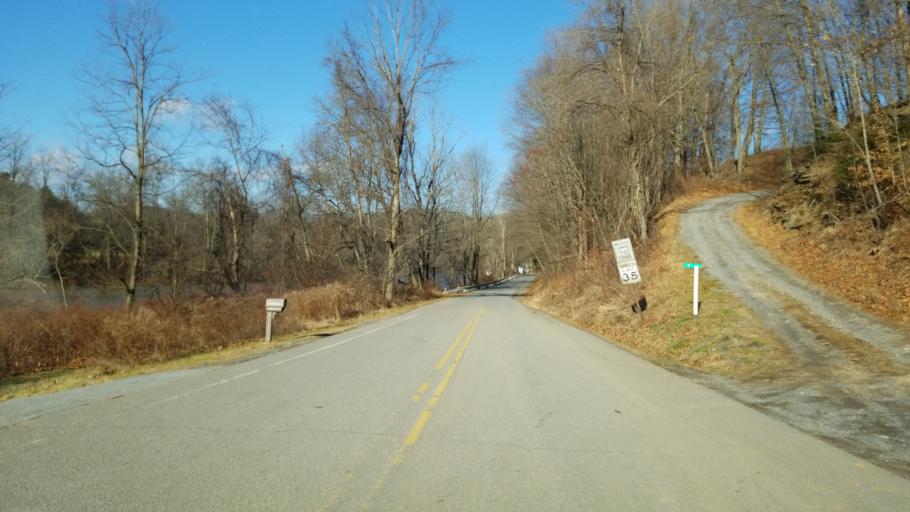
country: US
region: Pennsylvania
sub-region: Clearfield County
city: Curwensville
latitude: 40.9740
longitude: -78.4897
